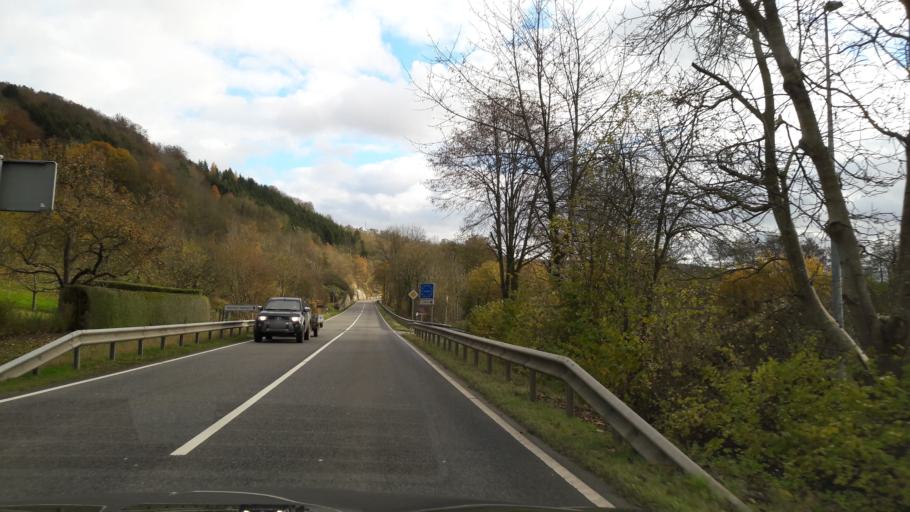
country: DE
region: Rheinland-Pfalz
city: Ralingen
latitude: 49.8115
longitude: 6.5023
